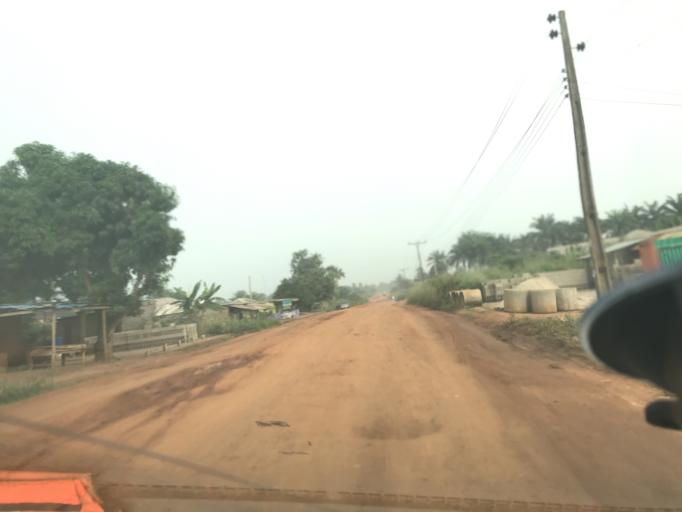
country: NG
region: Ogun
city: Ado Odo
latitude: 6.5386
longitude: 2.9498
